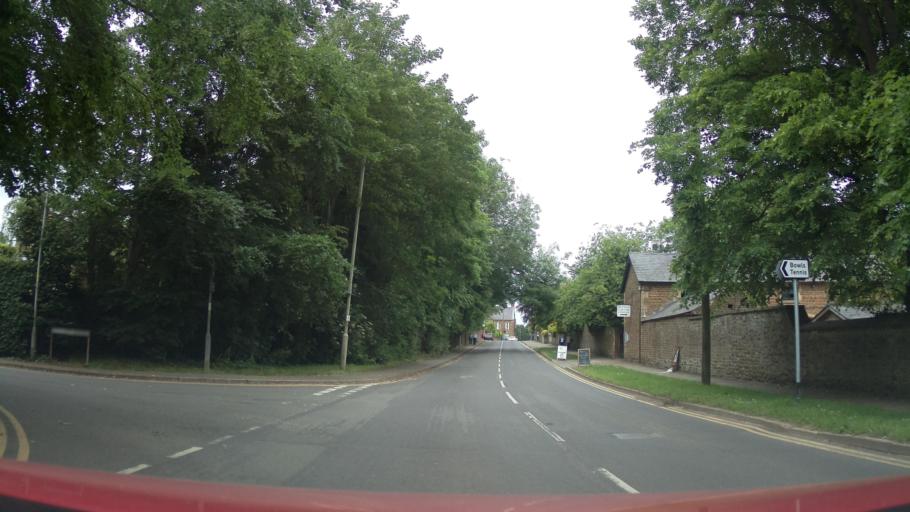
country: GB
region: England
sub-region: District of Rutland
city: Oakham
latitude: 52.6656
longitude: -0.7248
